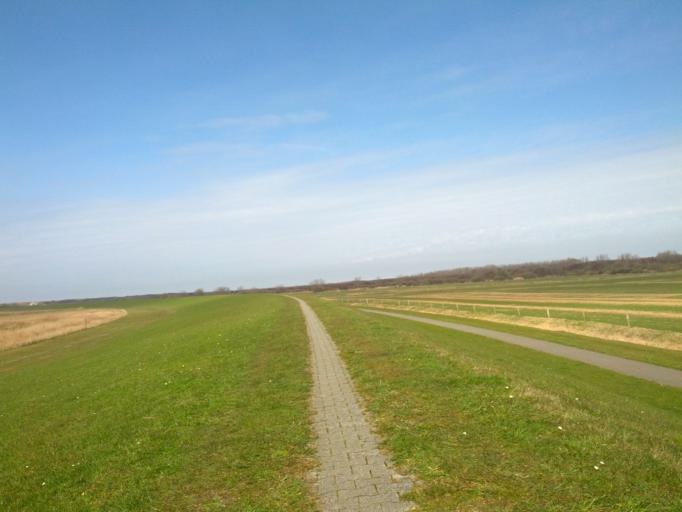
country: DE
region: Lower Saxony
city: Langeoog
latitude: 53.7273
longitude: 7.4872
